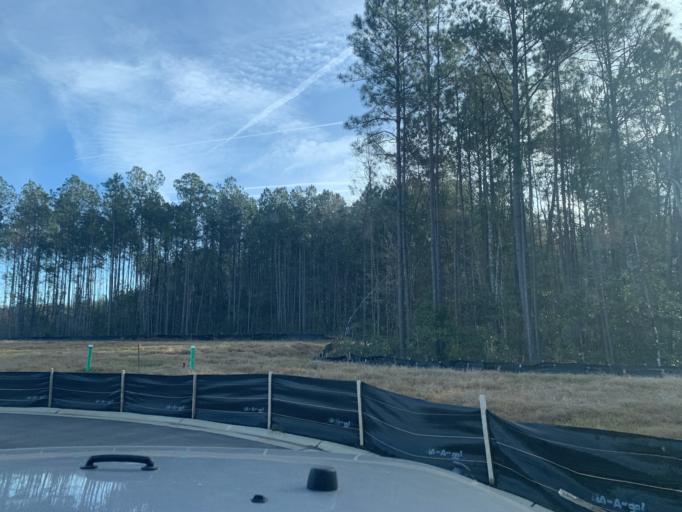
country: US
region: Georgia
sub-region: Chatham County
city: Pooler
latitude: 32.0652
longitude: -81.2571
